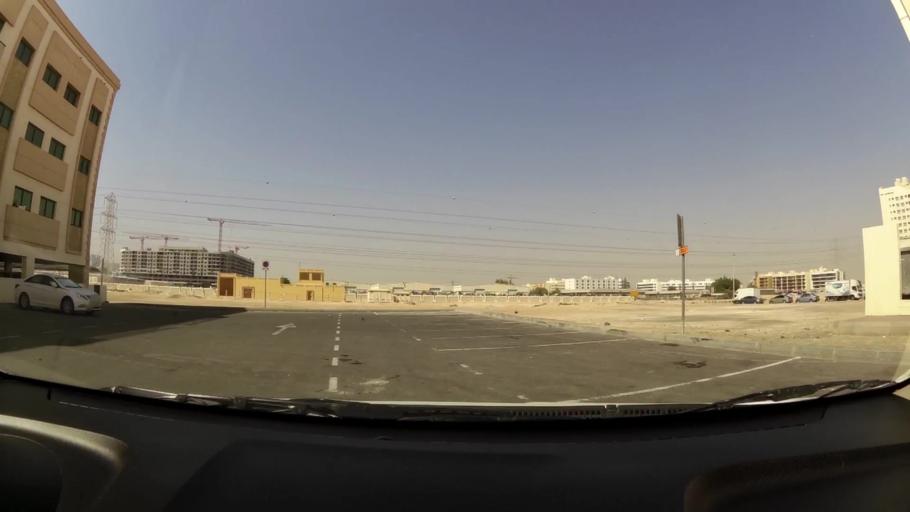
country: AE
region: Ash Shariqah
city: Sharjah
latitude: 25.2767
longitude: 55.3798
